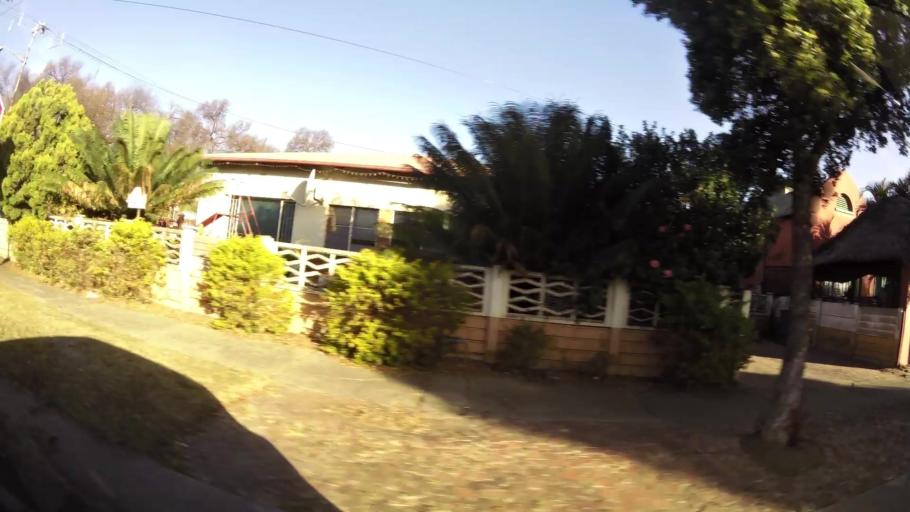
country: ZA
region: Gauteng
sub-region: City of Tshwane Metropolitan Municipality
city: Pretoria
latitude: -25.7244
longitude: 28.2080
